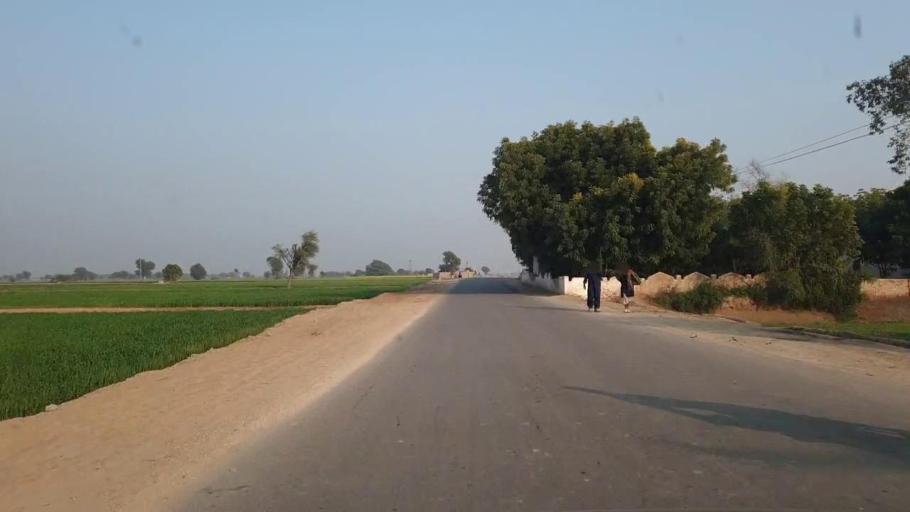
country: PK
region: Sindh
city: Bhit Shah
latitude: 25.8092
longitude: 68.4603
